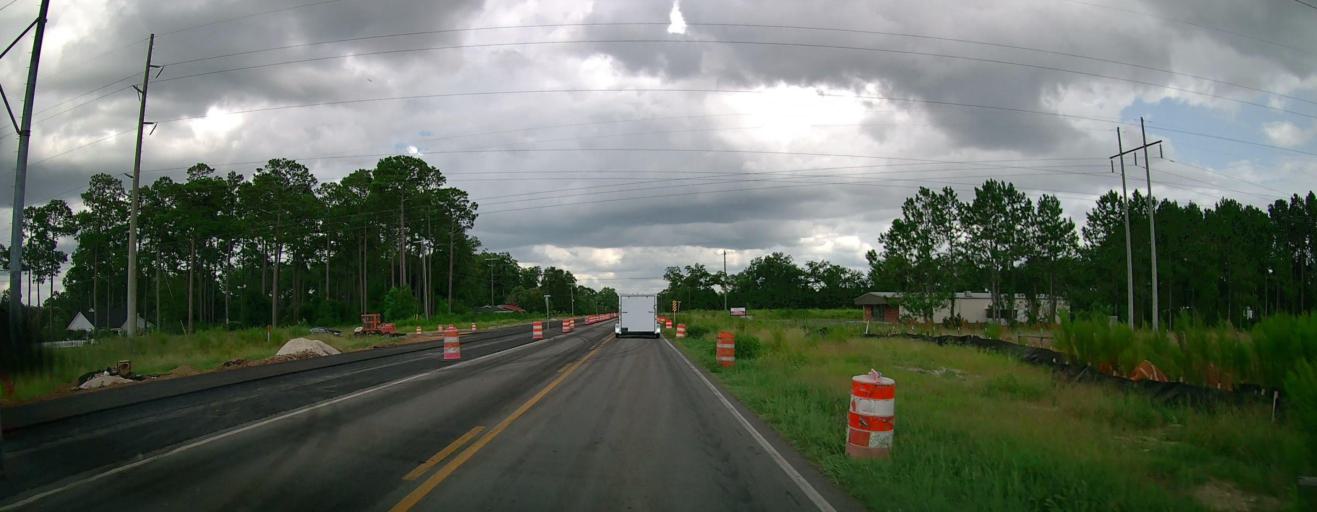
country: US
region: Georgia
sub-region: Coffee County
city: Douglas
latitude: 31.5188
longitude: -82.8868
